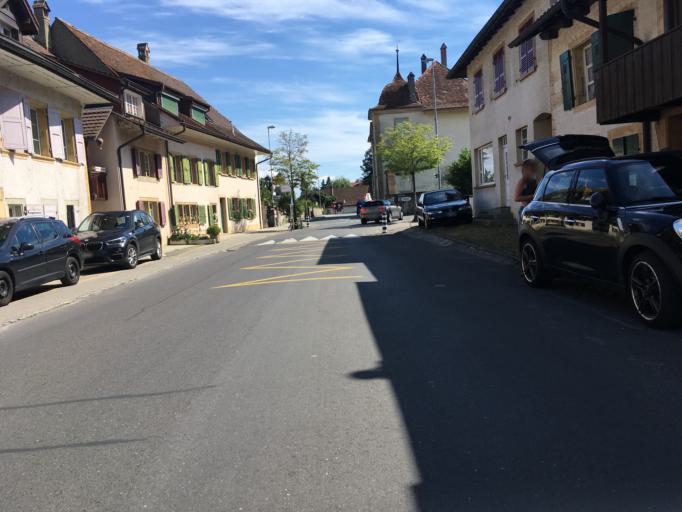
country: CH
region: Fribourg
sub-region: See District
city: Murten
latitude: 46.9350
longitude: 7.1232
